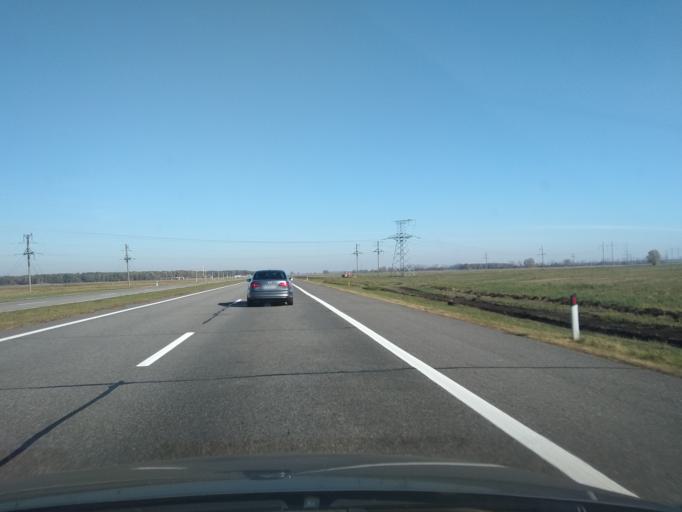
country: BY
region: Brest
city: Antopal'
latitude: 52.4027
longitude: 24.7962
